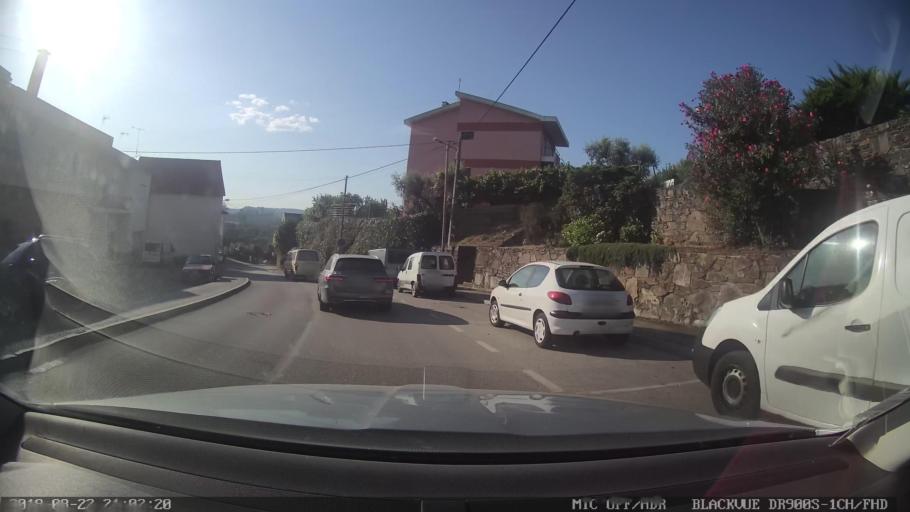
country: PT
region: Castelo Branco
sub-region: Serta
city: Serta
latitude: 39.8090
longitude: -8.0977
